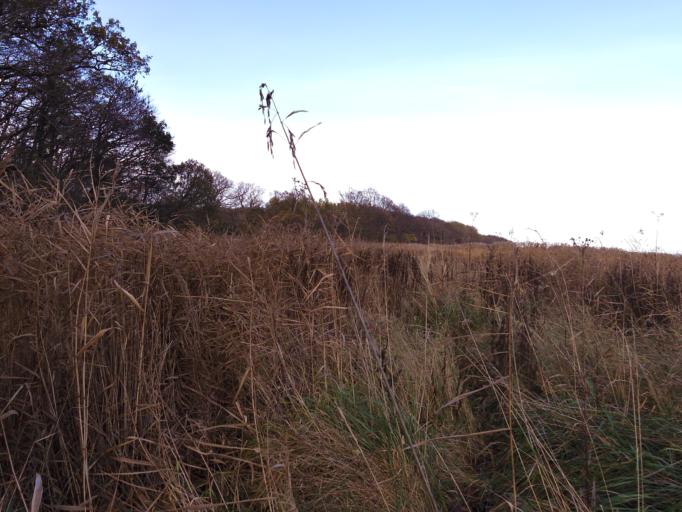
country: DK
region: Central Jutland
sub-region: Odder Kommune
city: Odder
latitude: 55.9045
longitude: 10.2325
